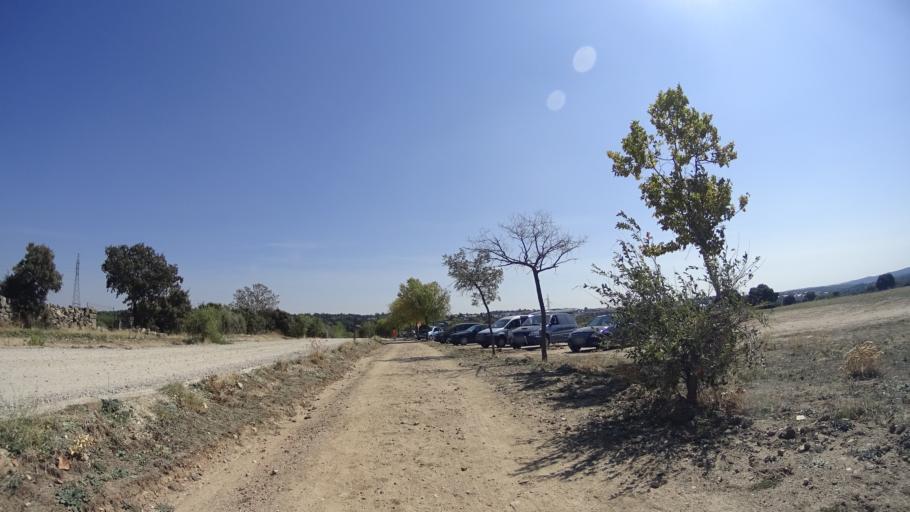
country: ES
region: Madrid
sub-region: Provincia de Madrid
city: Colmenarejo
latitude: 40.5688
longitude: -4.0268
